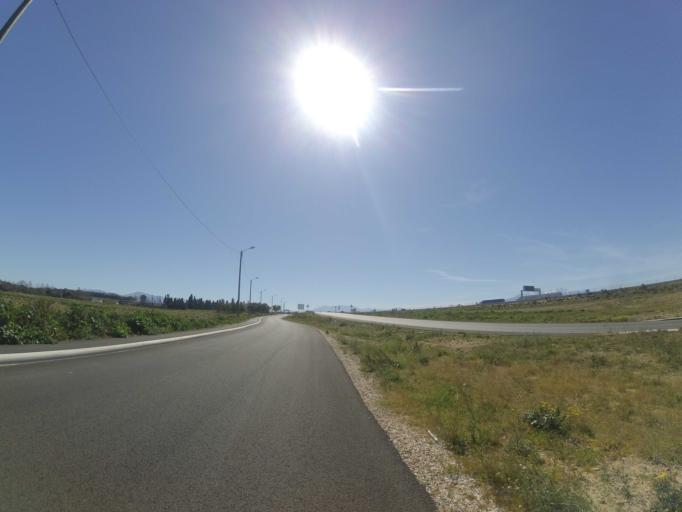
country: FR
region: Languedoc-Roussillon
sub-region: Departement des Pyrenees-Orientales
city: Saint-Esteve
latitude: 42.6826
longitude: 2.8638
